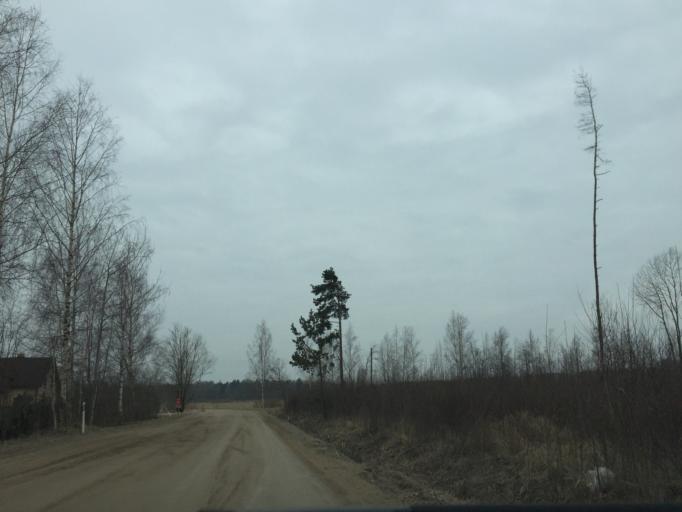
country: LV
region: Kekava
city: Kekava
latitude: 56.8036
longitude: 24.1667
